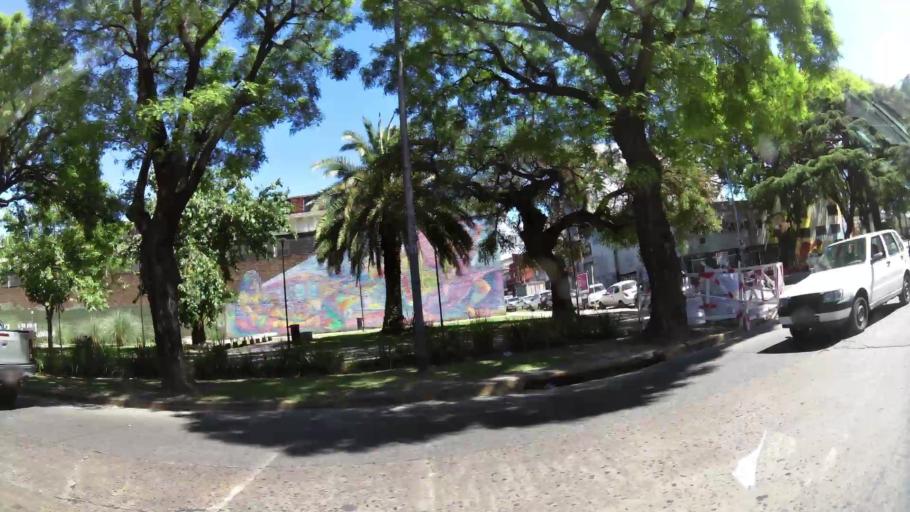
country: AR
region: Buenos Aires
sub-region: Partido de General San Martin
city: General San Martin
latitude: -34.5808
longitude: -58.5326
